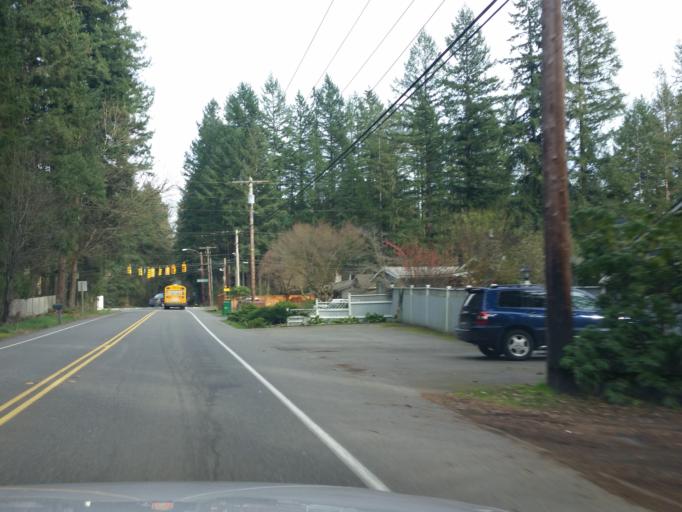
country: US
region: Washington
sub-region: King County
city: Cottage Lake
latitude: 47.7475
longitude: -122.0837
